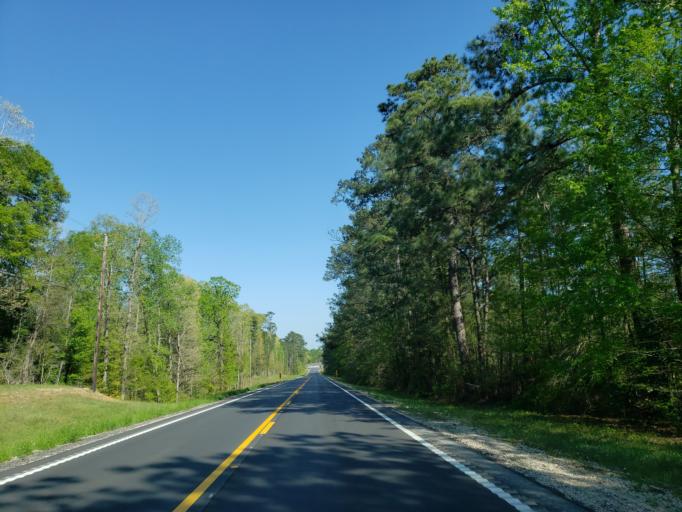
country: US
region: Mississippi
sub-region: Perry County
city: New Augusta
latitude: 31.1841
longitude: -88.9499
